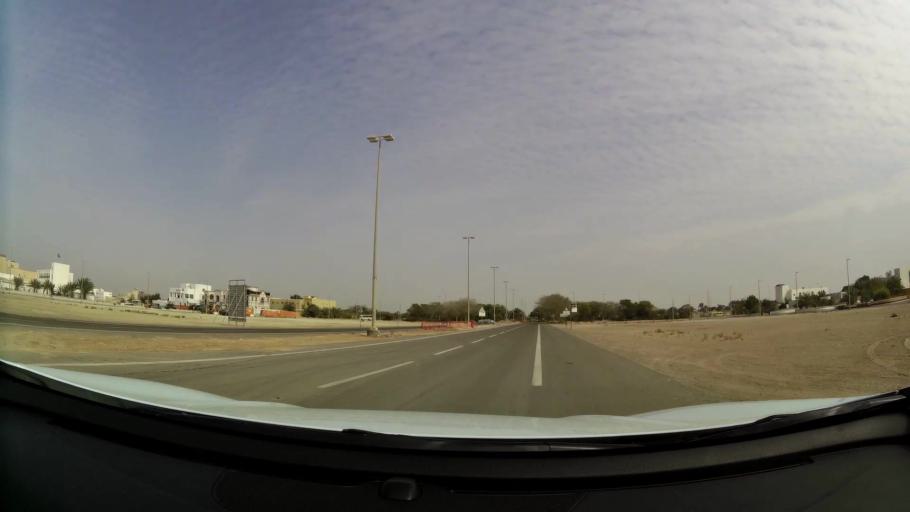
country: AE
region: Abu Dhabi
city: Abu Dhabi
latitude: 24.5807
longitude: 54.6928
